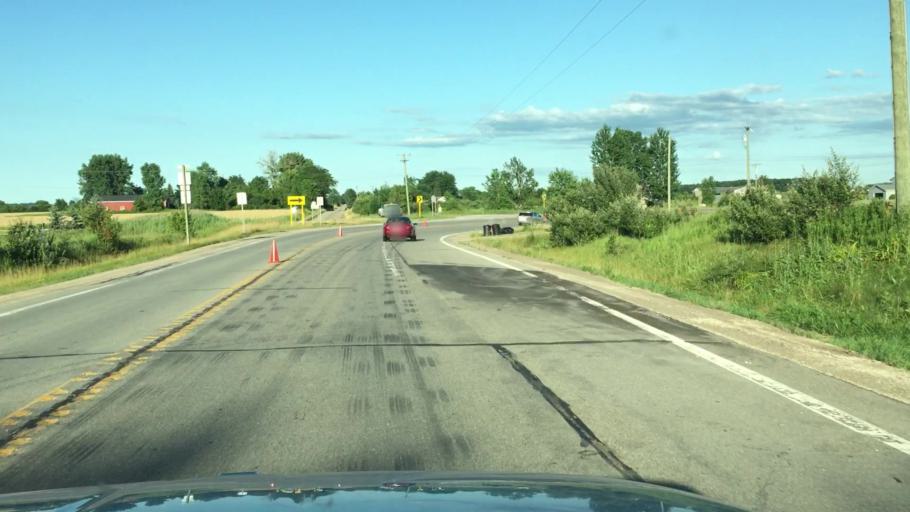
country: US
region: Michigan
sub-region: Saint Clair County
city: Yale
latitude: 43.1018
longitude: -82.7687
